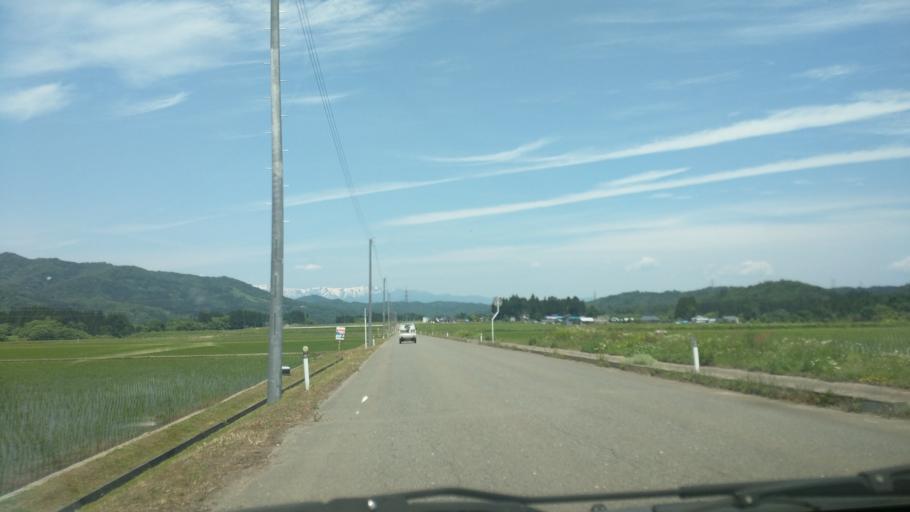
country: JP
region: Fukushima
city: Kitakata
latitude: 37.5045
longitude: 139.7179
